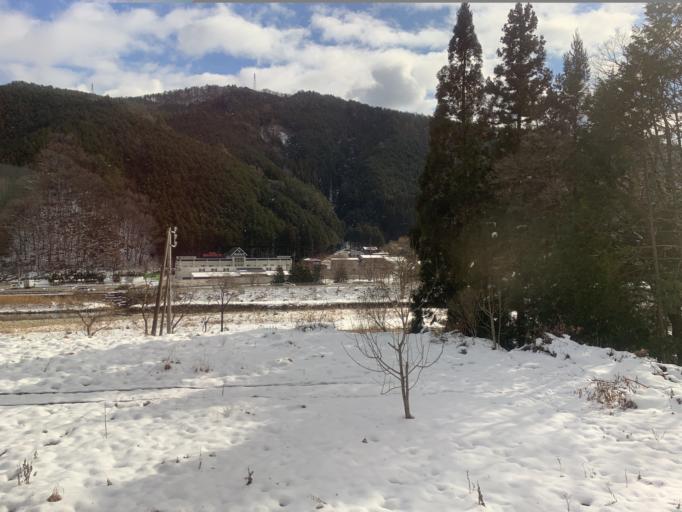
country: JP
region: Gifu
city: Takayama
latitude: 36.0921
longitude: 137.2518
